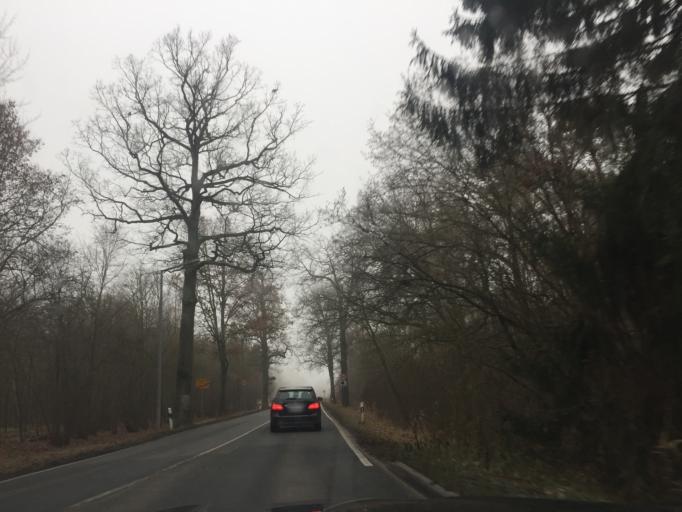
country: DE
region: Brandenburg
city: Falkensee
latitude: 52.5960
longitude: 13.1007
